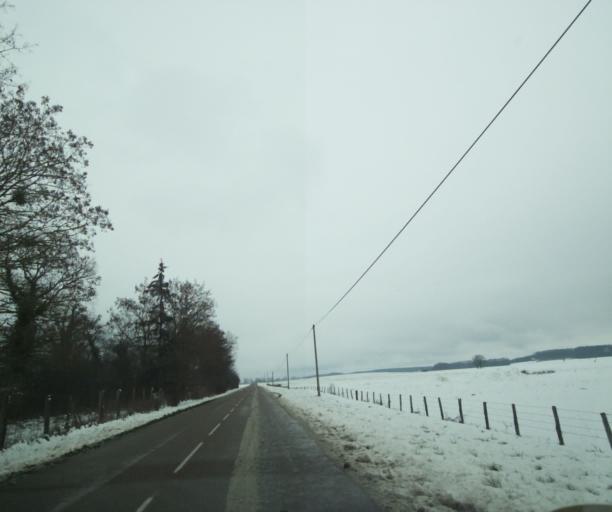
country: FR
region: Champagne-Ardenne
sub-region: Departement de la Haute-Marne
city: Montier-en-Der
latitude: 48.4515
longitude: 4.7773
